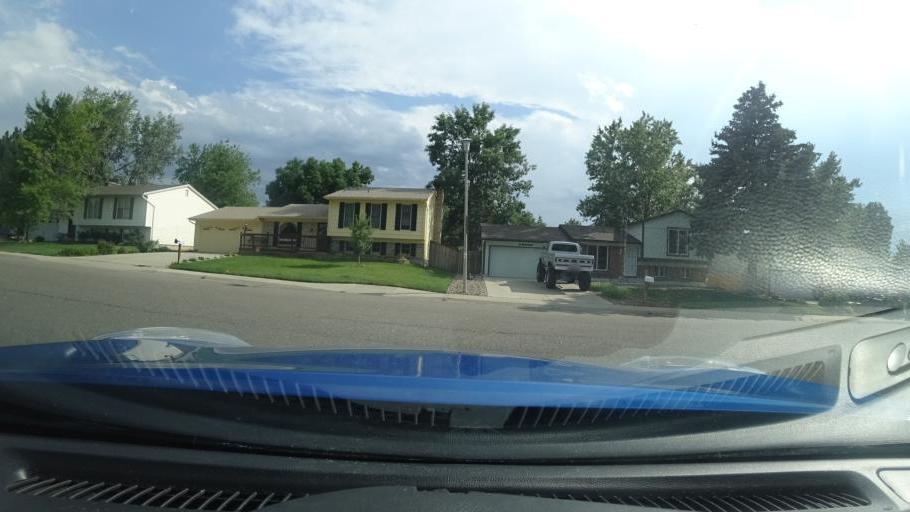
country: US
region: Colorado
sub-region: Adams County
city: Aurora
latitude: 39.6915
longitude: -104.7981
